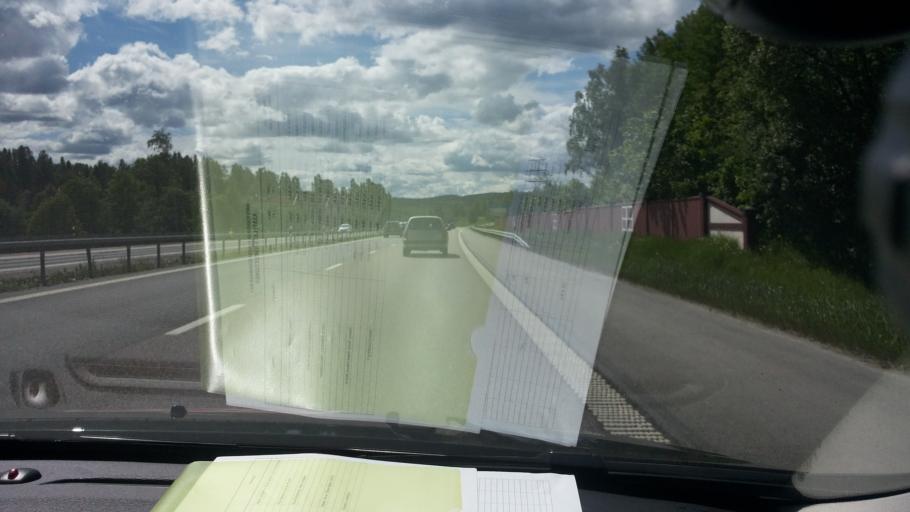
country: SE
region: Vaesternorrland
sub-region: Timra Kommun
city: Timra
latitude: 62.4848
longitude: 17.3206
